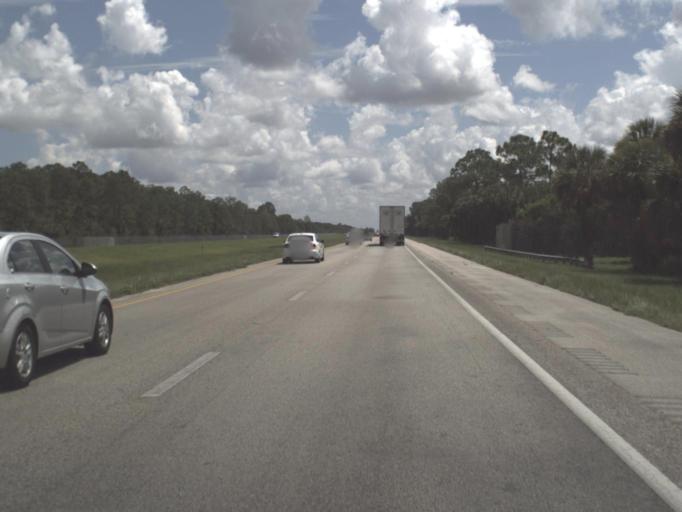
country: US
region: Florida
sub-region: Collier County
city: Orangetree
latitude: 26.1531
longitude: -81.4617
